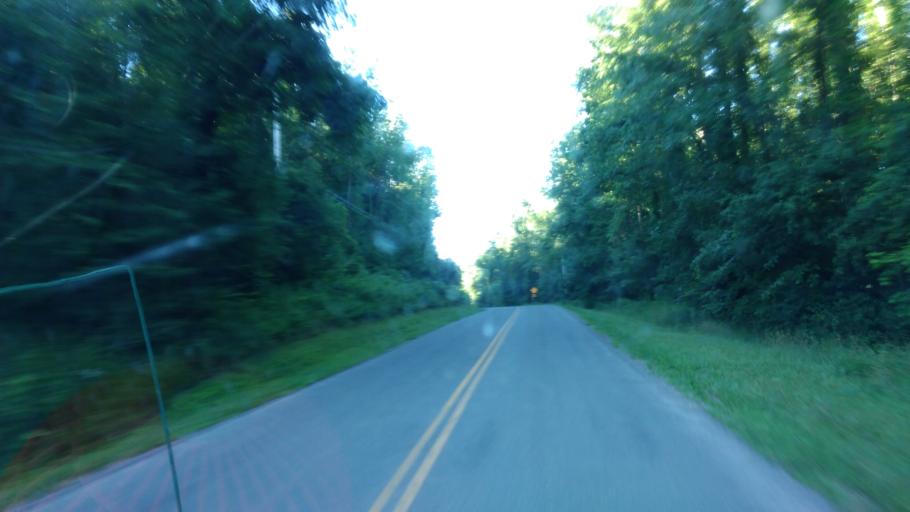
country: US
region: New York
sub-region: Wayne County
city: Lyons
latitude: 43.0909
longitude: -77.0228
